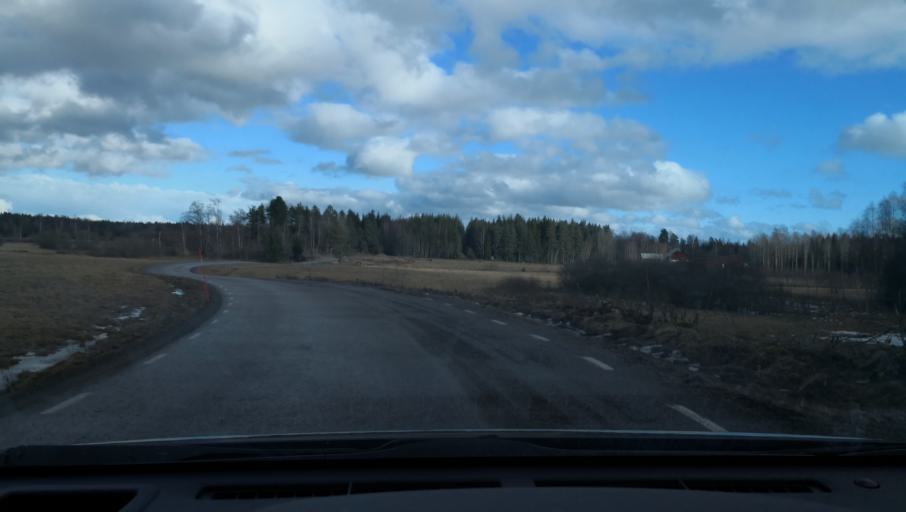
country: SE
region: OErebro
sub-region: Lindesbergs Kommun
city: Fellingsbro
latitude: 59.3389
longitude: 15.6966
